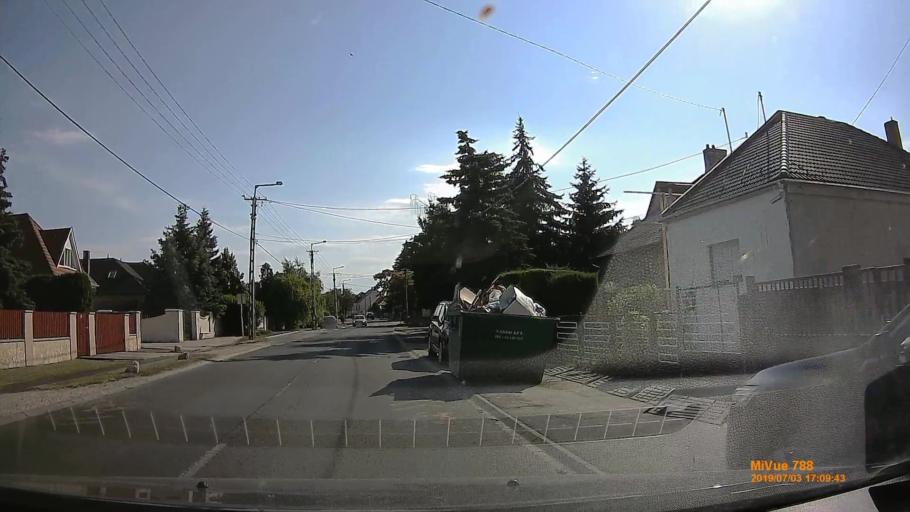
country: HU
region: Gyor-Moson-Sopron
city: Gyor
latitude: 47.7070
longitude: 17.6459
